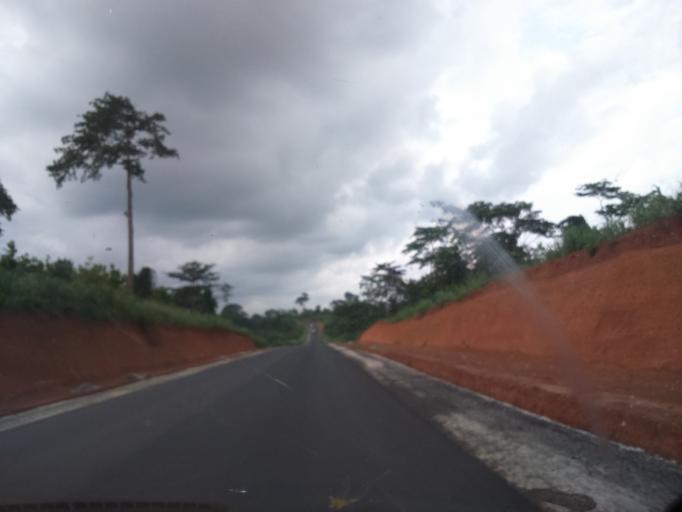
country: CI
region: Lagunes
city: Akoupe
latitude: 6.5050
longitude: -3.8209
